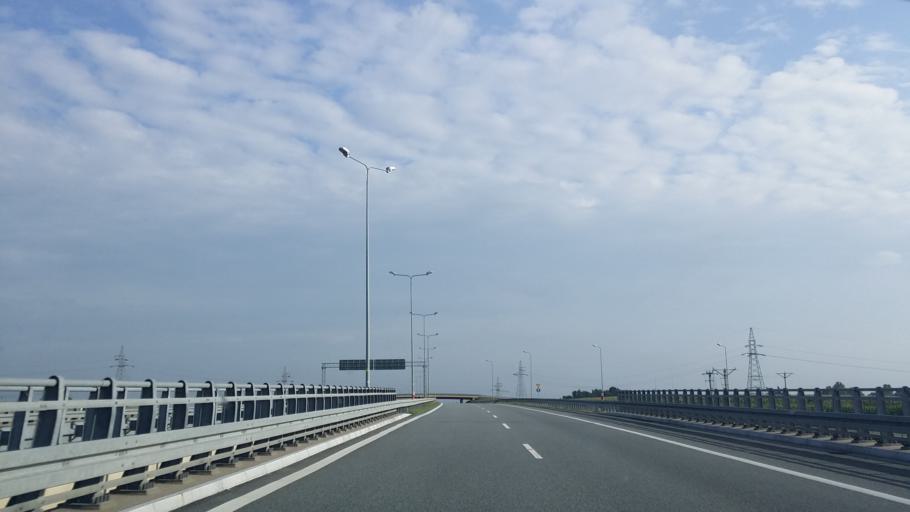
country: PL
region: Lubusz
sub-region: Powiat swiebodzinski
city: Swiebodzin
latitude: 52.2753
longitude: 15.5391
